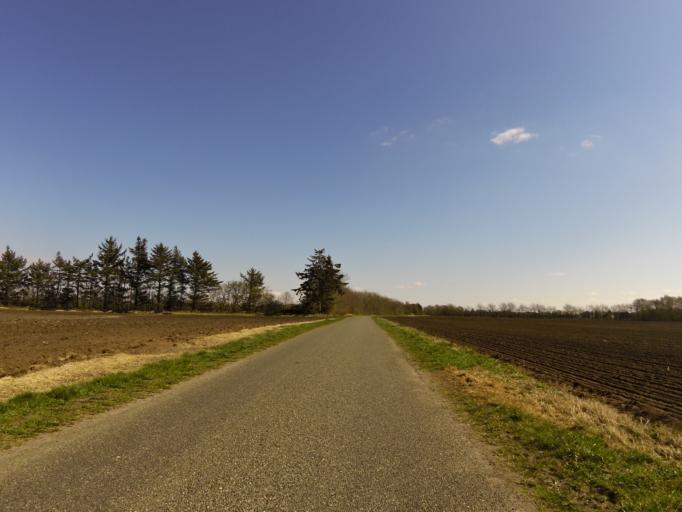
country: DK
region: South Denmark
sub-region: Esbjerg Kommune
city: Ribe
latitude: 55.3378
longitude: 8.8741
